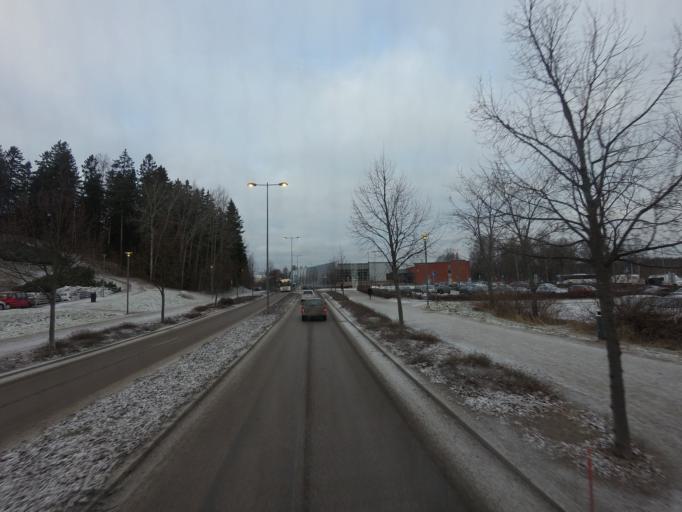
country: FI
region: Uusimaa
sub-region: Helsinki
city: Espoo
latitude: 60.2086
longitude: 24.6602
